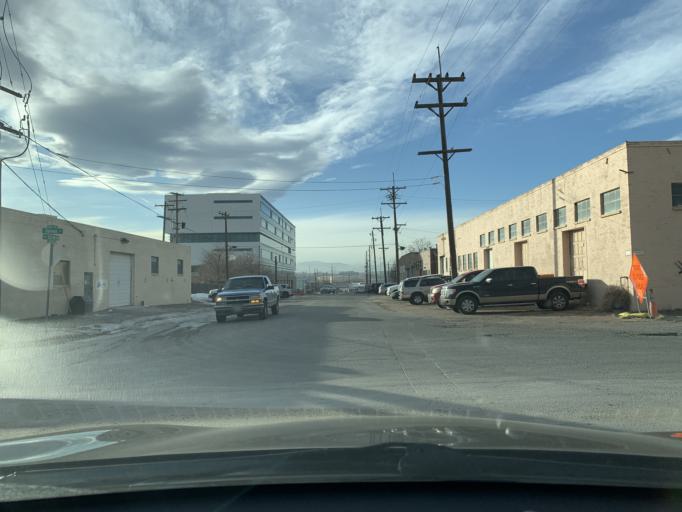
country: US
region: Colorado
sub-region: Denver County
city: Denver
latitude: 39.7353
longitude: -105.0077
